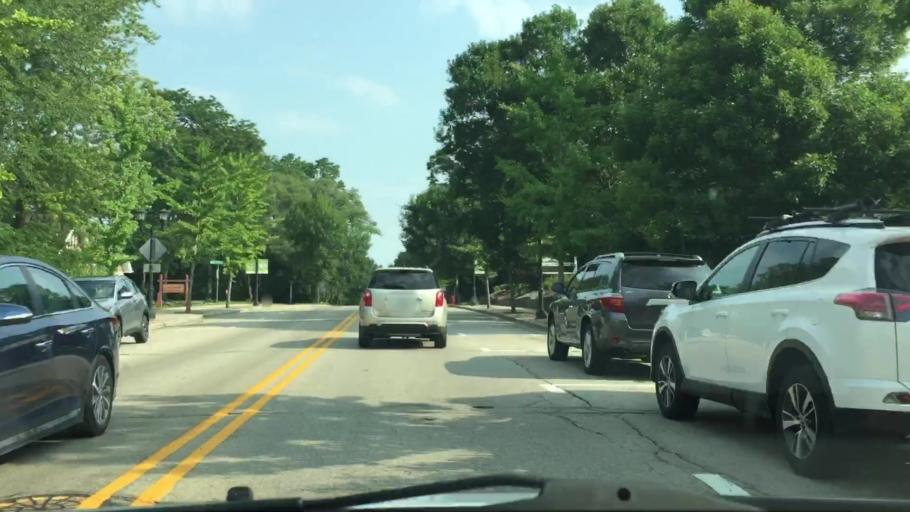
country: US
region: Wisconsin
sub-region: Waukesha County
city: Brookfield
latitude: 43.0735
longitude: -88.1459
